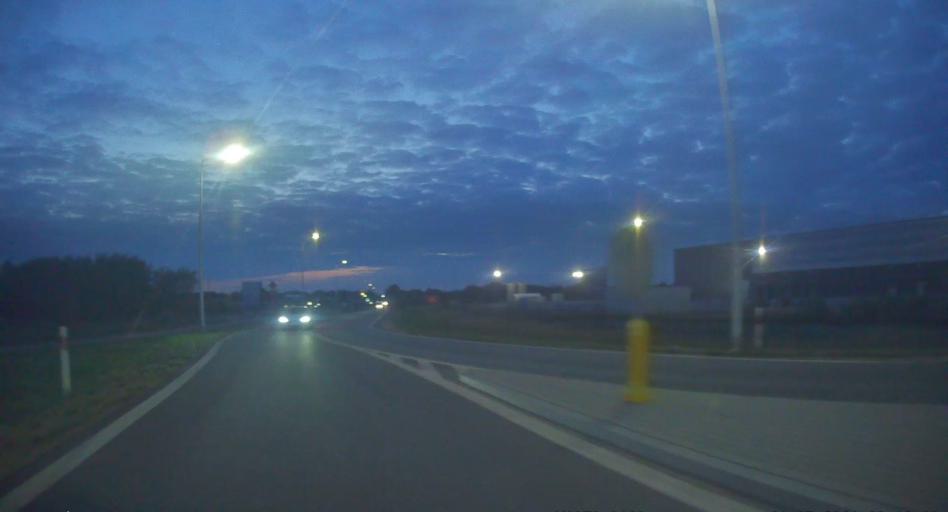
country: PL
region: Silesian Voivodeship
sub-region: Powiat klobucki
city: Kamyk
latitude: 50.8761
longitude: 19.0009
